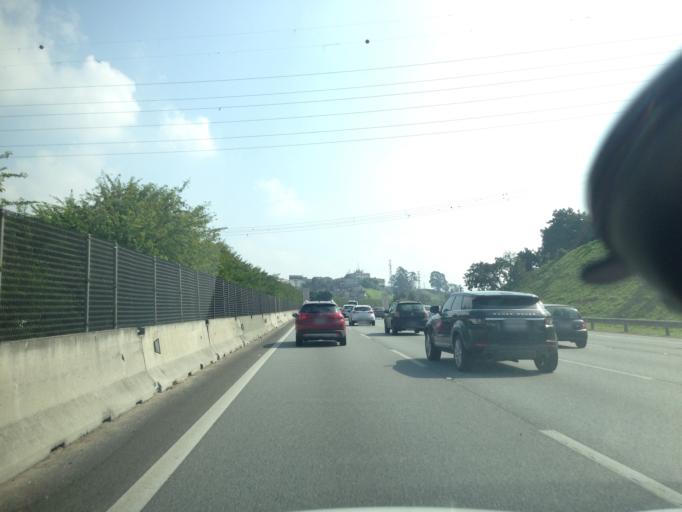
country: BR
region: Sao Paulo
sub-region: Diadema
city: Diadema
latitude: -23.6762
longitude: -46.6235
